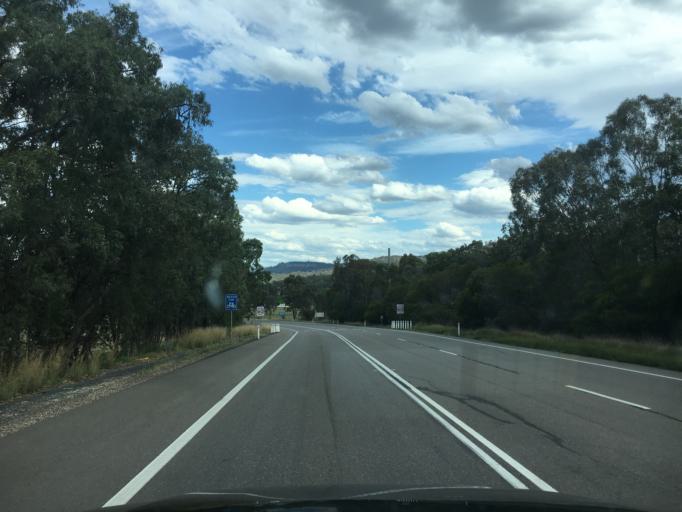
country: AU
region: New South Wales
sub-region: Liverpool Plains
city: Quirindi
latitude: -31.7552
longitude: 150.8165
